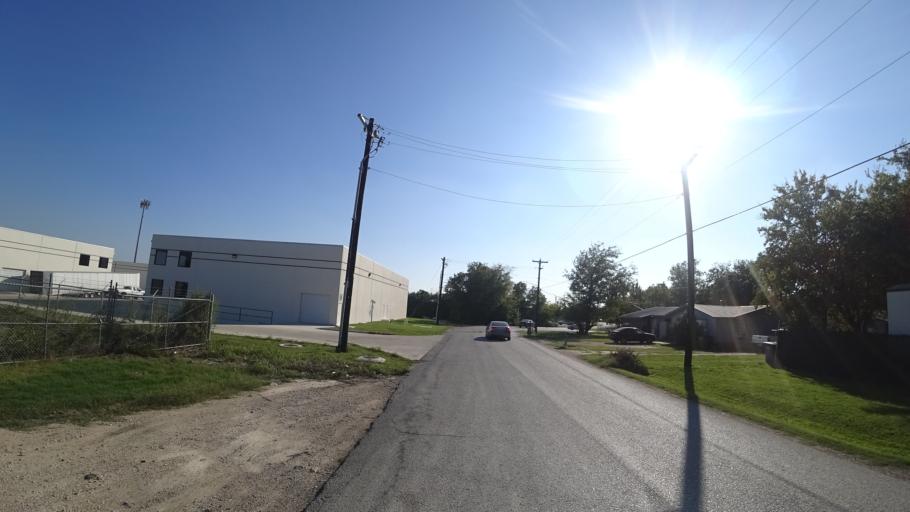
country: US
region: Texas
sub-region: Travis County
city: Wells Branch
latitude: 30.3505
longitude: -97.6698
